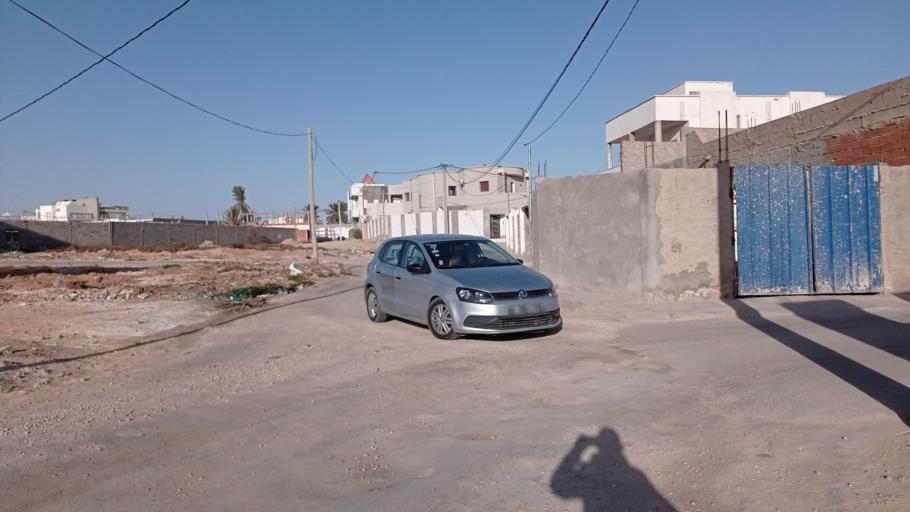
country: TN
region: Qabis
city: Gabes
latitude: 33.8534
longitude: 10.1203
